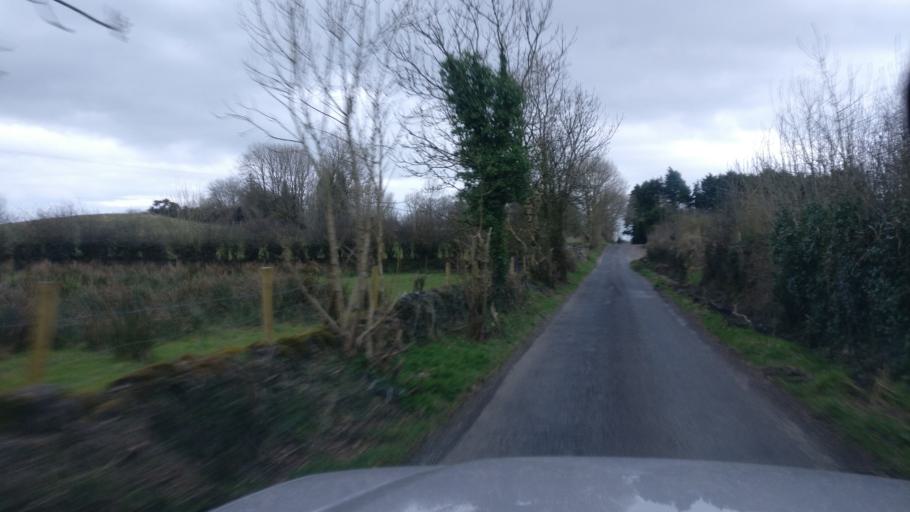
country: IE
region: Connaught
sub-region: County Galway
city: Loughrea
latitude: 53.2615
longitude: -8.4547
